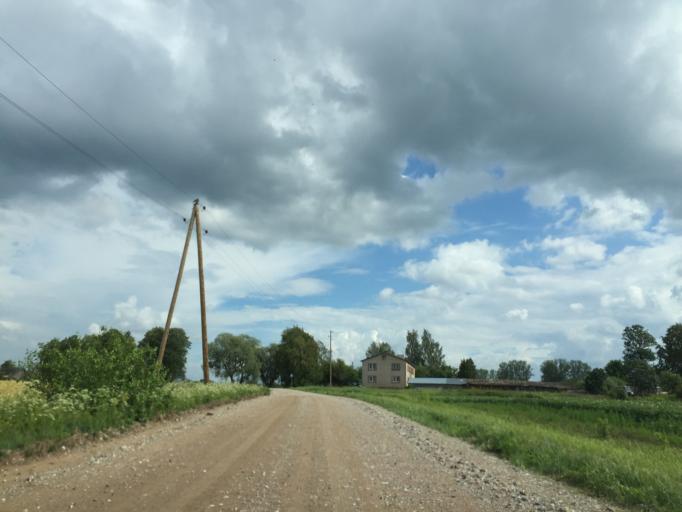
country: LV
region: Ligatne
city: Ligatne
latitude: 57.2117
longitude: 24.9562
